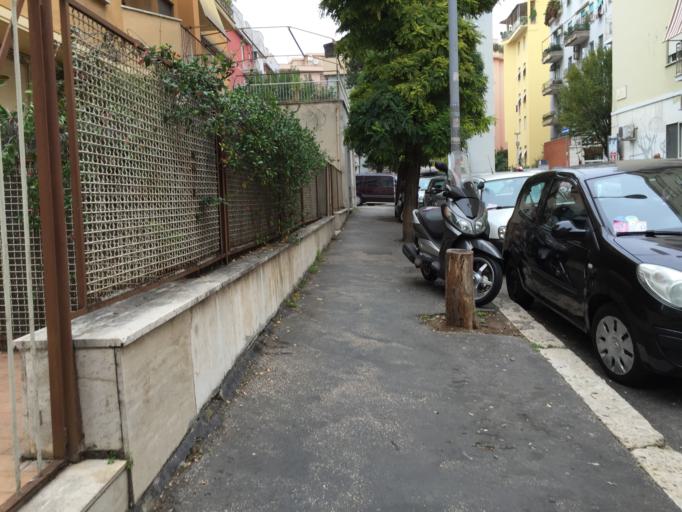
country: VA
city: Vatican City
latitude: 41.8694
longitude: 12.4450
